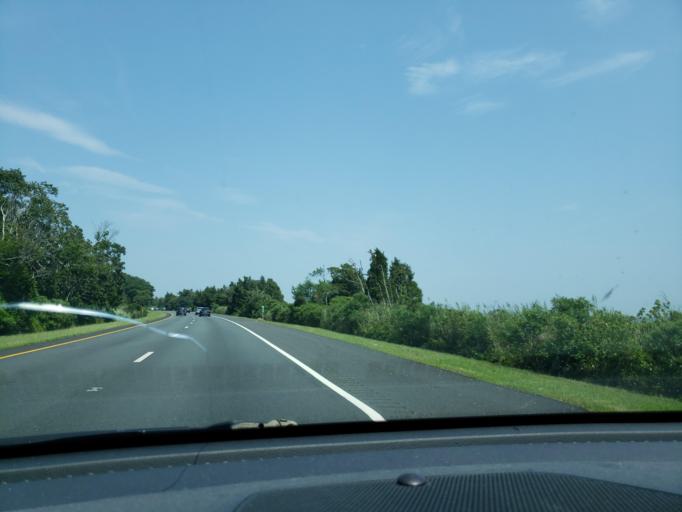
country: US
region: New Jersey
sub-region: Cape May County
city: Ocean City
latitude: 39.2734
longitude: -74.6308
